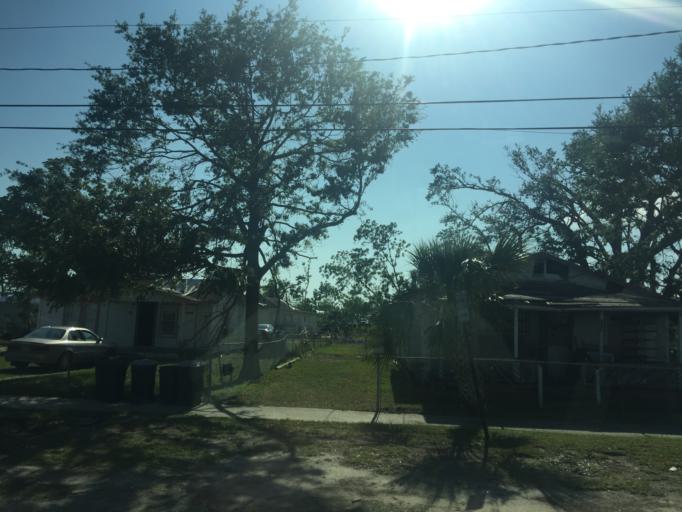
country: US
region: Florida
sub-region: Bay County
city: Springfield
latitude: 30.1589
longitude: -85.6165
